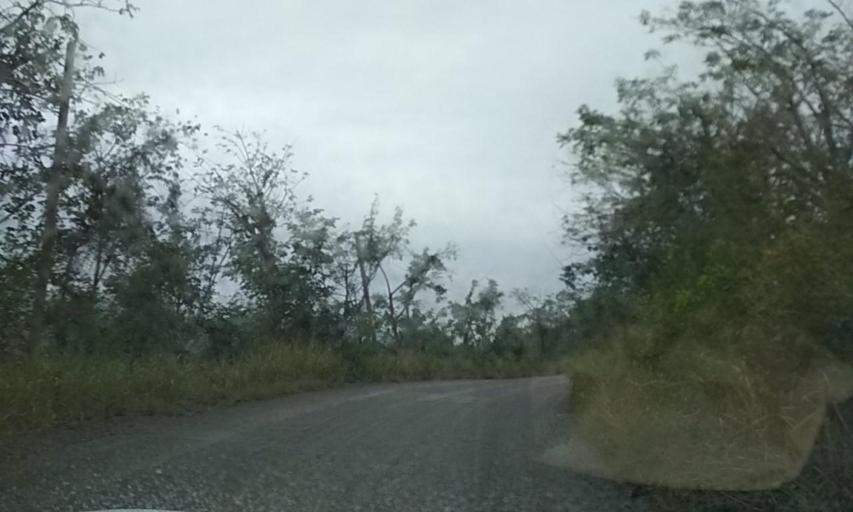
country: MX
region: Veracruz
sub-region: Coatzintla
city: Manuel Maria Contreras
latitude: 20.4524
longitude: -97.4749
